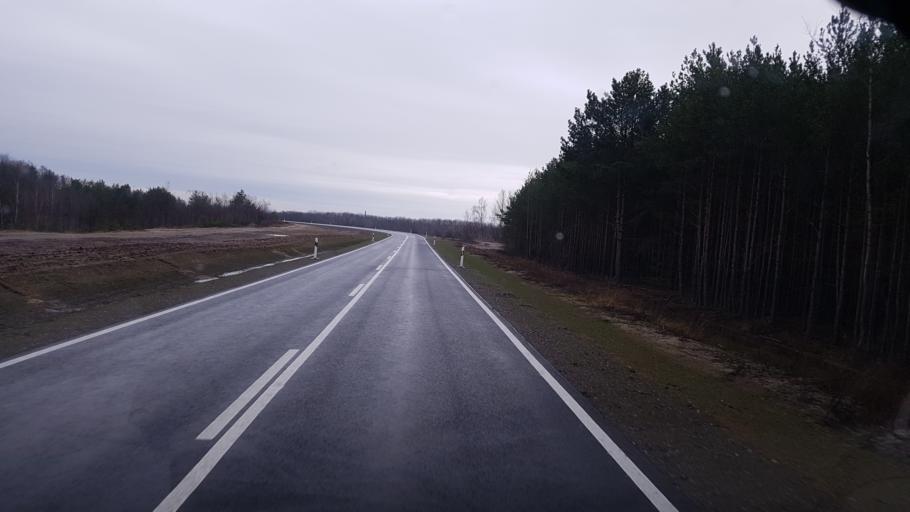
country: DE
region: Brandenburg
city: Lauchhammer
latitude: 51.5176
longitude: 13.7941
